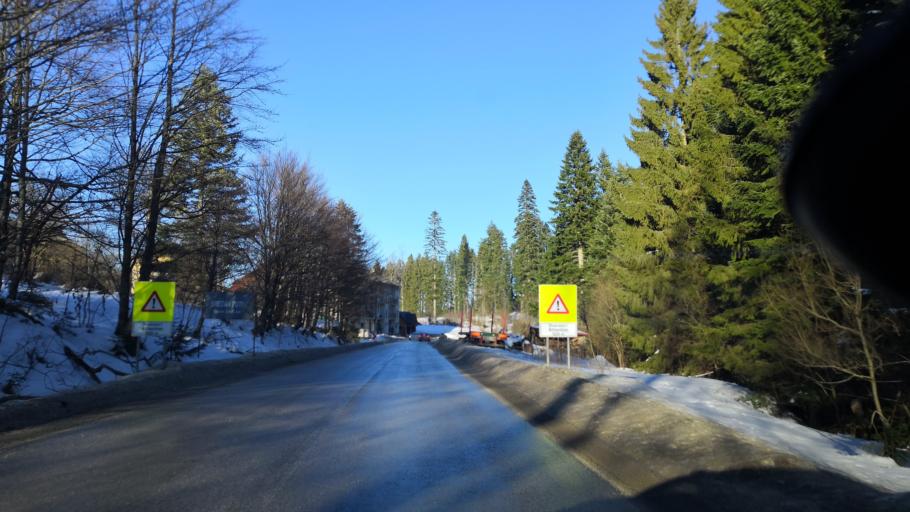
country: BA
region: Republika Srpska
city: Han Pijesak
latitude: 44.0757
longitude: 18.9503
